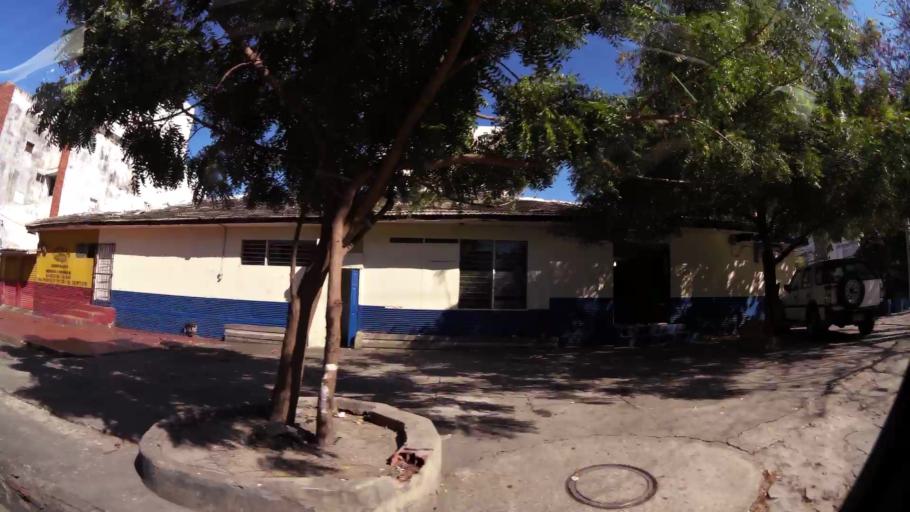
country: CO
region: Atlantico
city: Barranquilla
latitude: 11.0016
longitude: -74.8212
